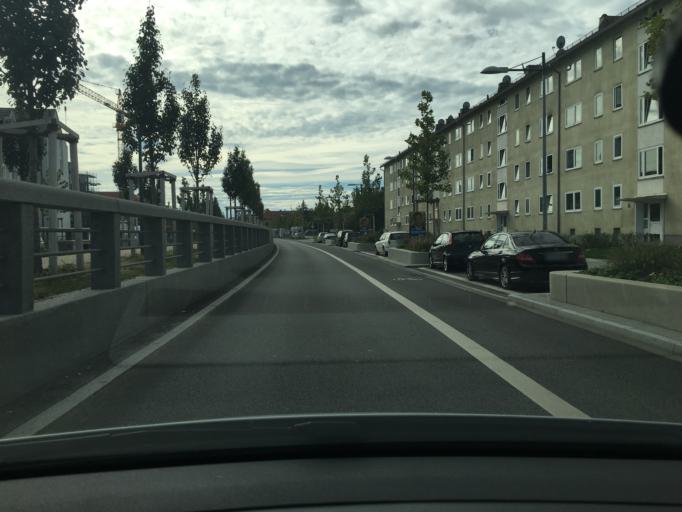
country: DE
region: Bavaria
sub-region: Upper Bavaria
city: Pullach im Isartal
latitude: 48.1175
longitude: 11.5169
